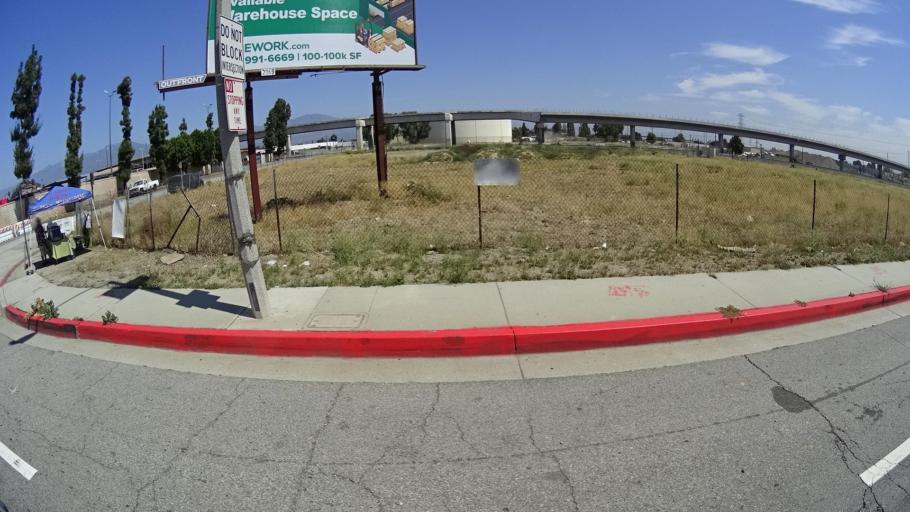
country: US
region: California
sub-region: Los Angeles County
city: El Monte
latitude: 34.0588
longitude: -118.0107
